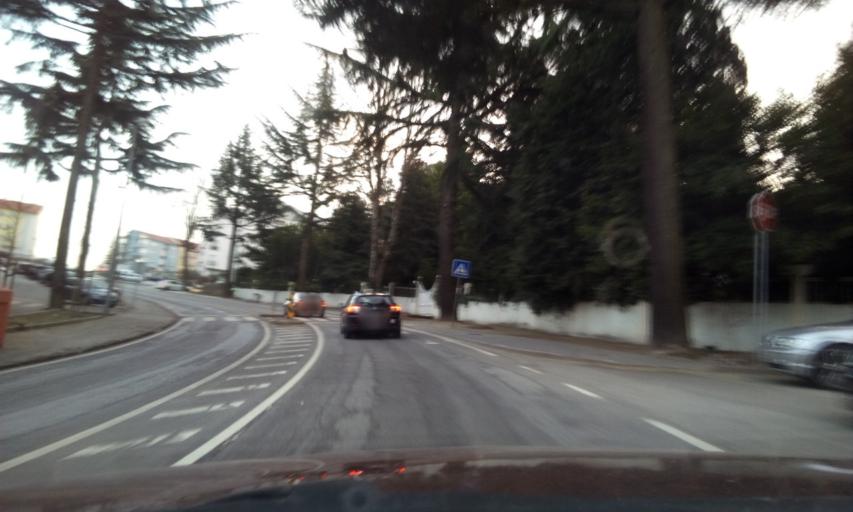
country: PT
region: Guarda
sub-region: Guarda
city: Guarda
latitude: 40.5467
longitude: -7.2528
